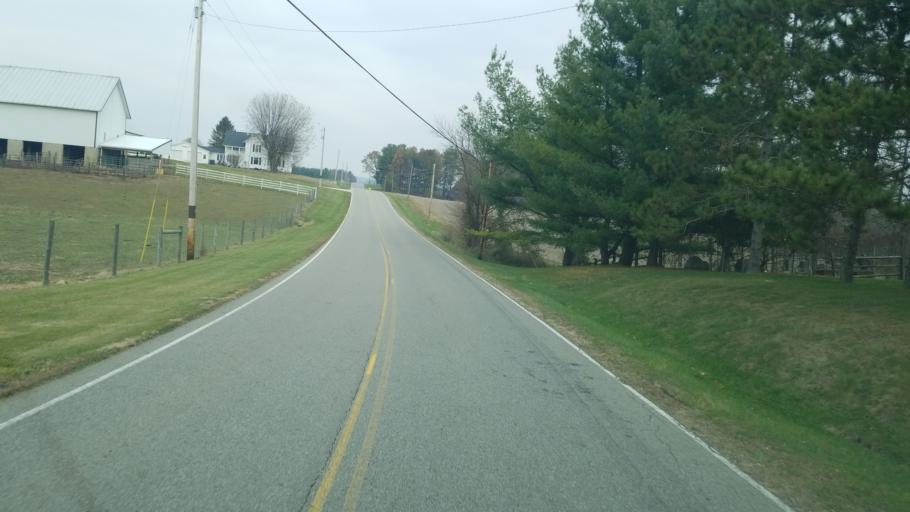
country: US
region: Ohio
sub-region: Licking County
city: Utica
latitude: 40.2129
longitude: -82.3667
